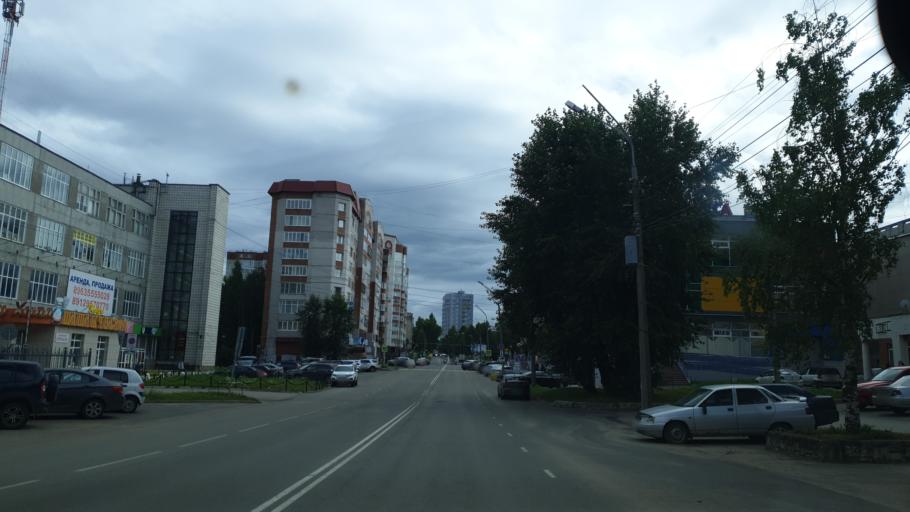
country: RU
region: Komi Republic
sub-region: Syktyvdinskiy Rayon
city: Syktyvkar
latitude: 61.6744
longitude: 50.8244
